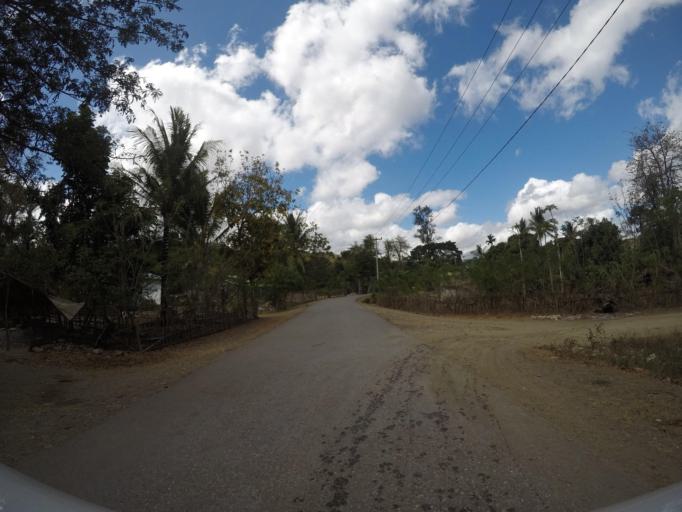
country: TL
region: Lautem
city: Lospalos
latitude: -8.4550
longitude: 126.8219
